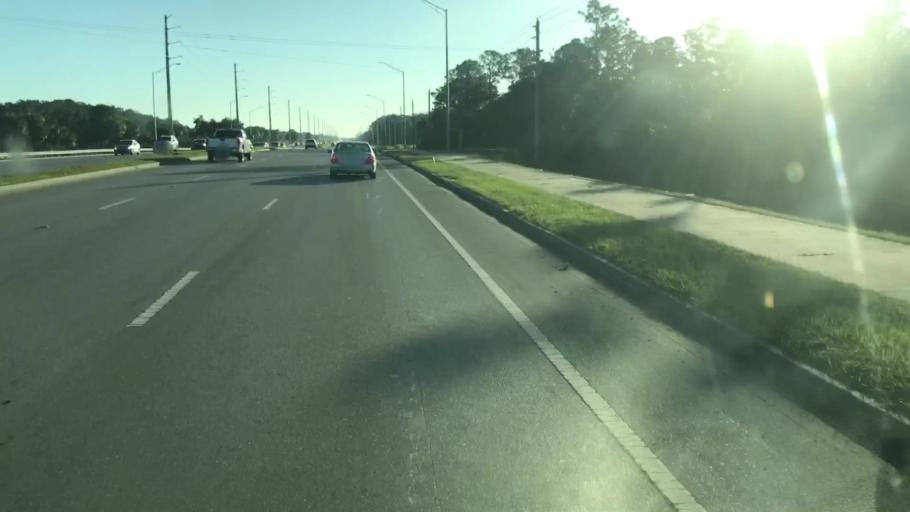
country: US
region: Florida
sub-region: Collier County
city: Orangetree
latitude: 26.2741
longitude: -81.6419
